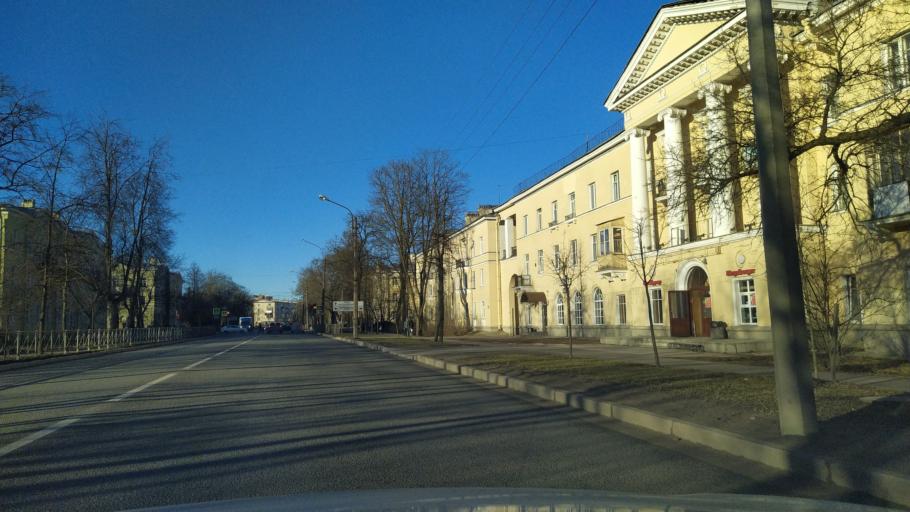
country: RU
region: St.-Petersburg
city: Krasnoye Selo
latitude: 59.7347
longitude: 30.0887
